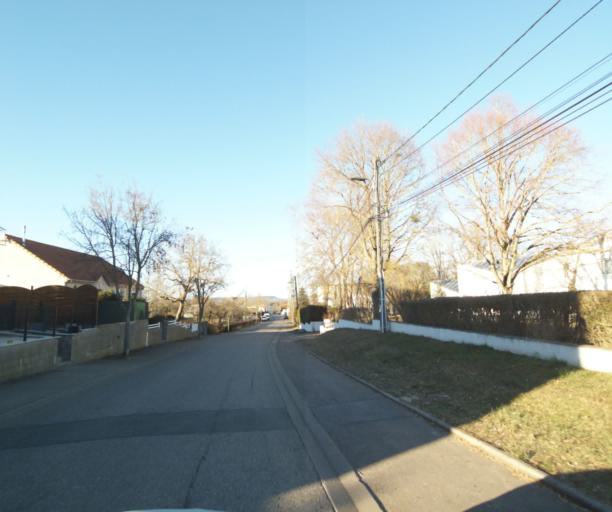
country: FR
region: Lorraine
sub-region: Departement de Meurthe-et-Moselle
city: Laneuveville-devant-Nancy
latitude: 48.6471
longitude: 6.2332
